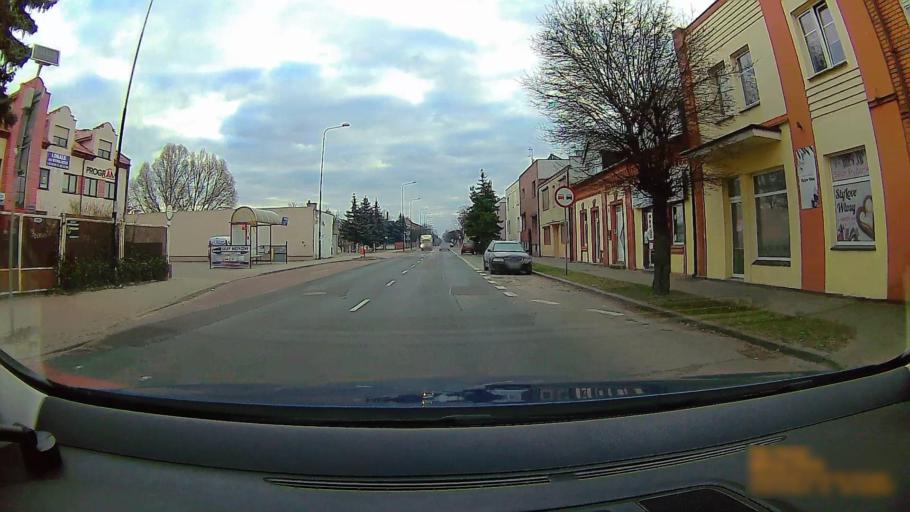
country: PL
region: Greater Poland Voivodeship
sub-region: Konin
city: Konin
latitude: 52.2044
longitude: 18.2559
